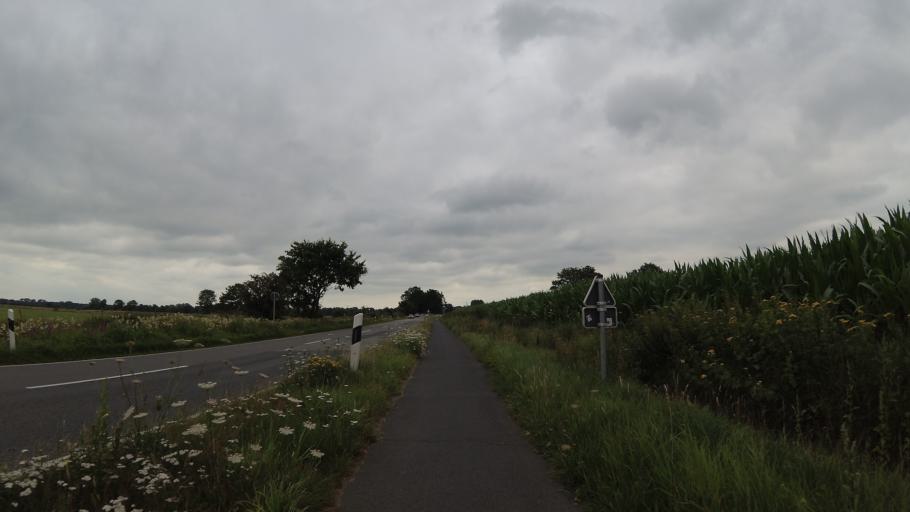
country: DE
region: Lower Saxony
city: Niederlangen
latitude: 52.8578
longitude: 7.2911
